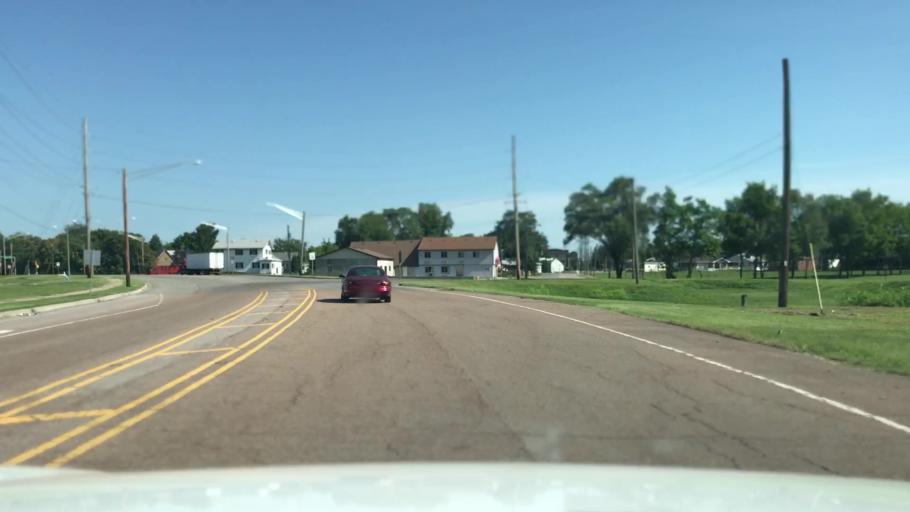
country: US
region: Illinois
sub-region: Madison County
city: Venice
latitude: 38.6687
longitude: -90.1703
